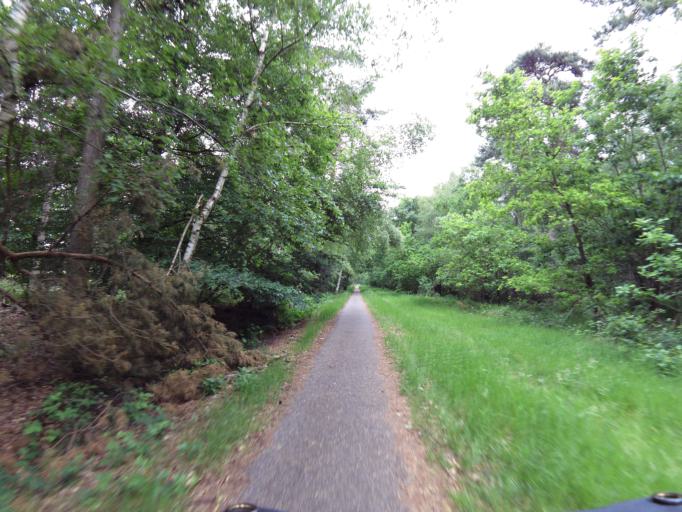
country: NL
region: North Brabant
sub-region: Gemeente Breda
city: Breda
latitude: 51.5427
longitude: 4.8327
